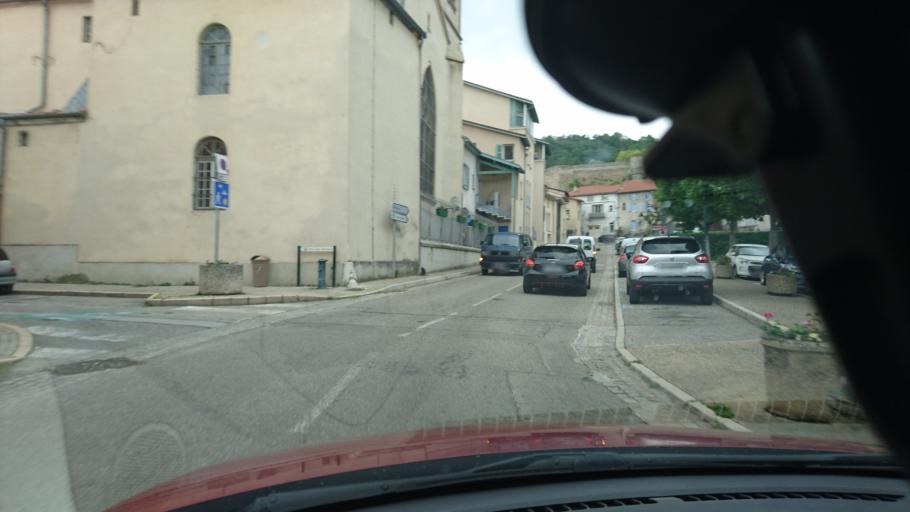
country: FR
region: Rhone-Alpes
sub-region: Departement du Rhone
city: Condrieu
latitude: 45.4634
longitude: 4.7684
